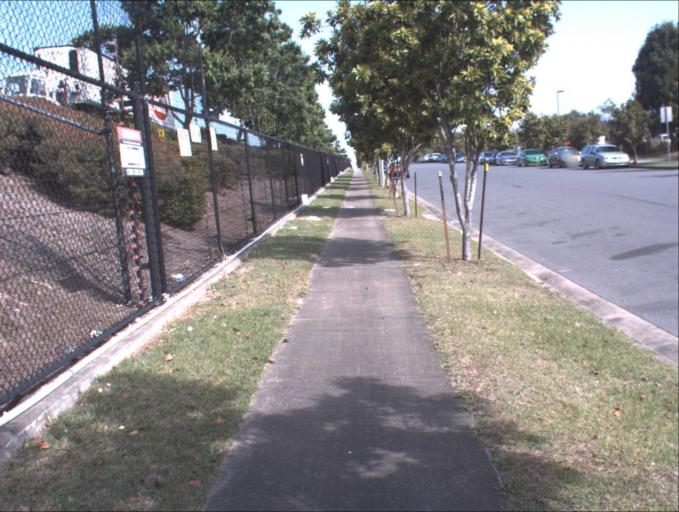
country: AU
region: Queensland
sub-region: Logan
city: Logan Reserve
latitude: -27.6878
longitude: 153.0748
